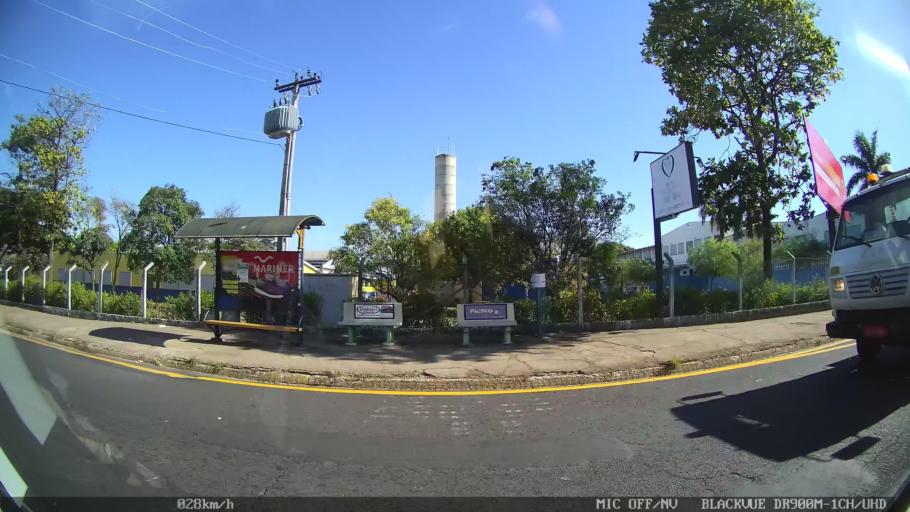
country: BR
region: Sao Paulo
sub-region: Franca
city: Franca
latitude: -20.5087
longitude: -47.4016
